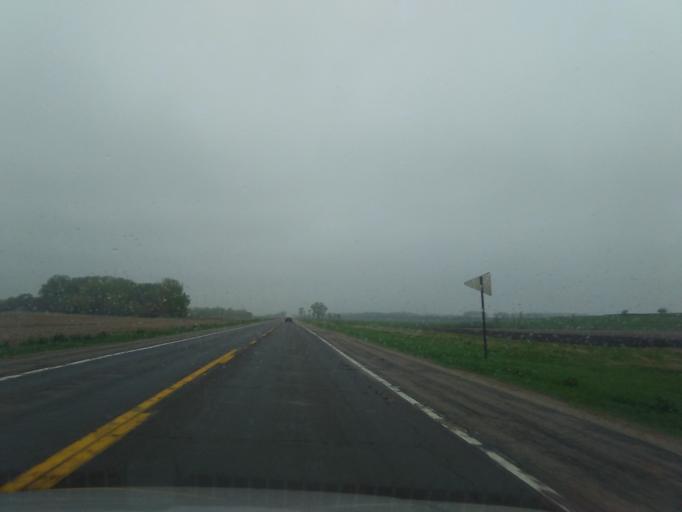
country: US
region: Nebraska
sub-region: Cuming County
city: Wisner
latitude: 41.9371
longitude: -96.8283
